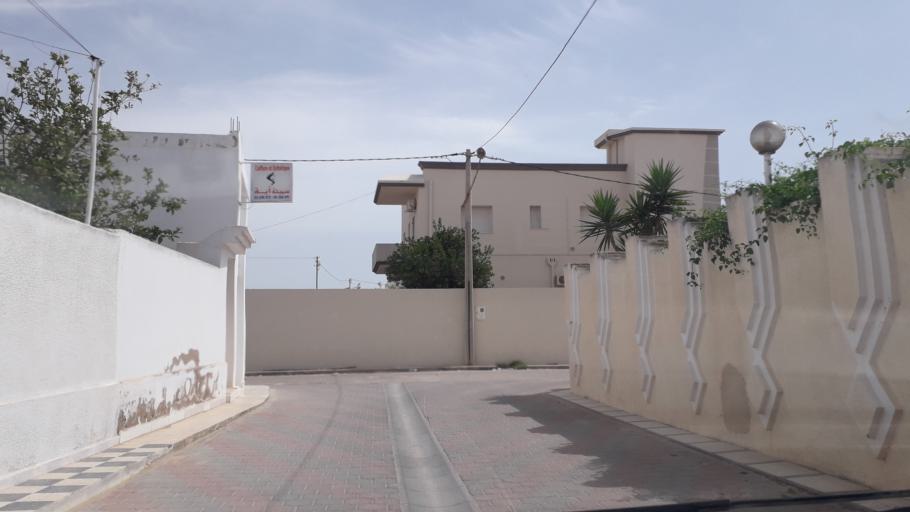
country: TN
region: Safaqis
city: Al Qarmadah
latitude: 34.8009
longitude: 10.7682
